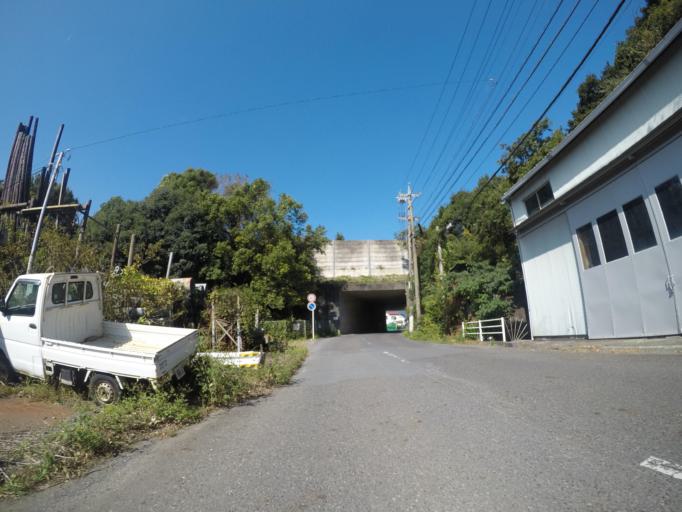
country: JP
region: Shizuoka
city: Shizuoka-shi
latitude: 35.0658
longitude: 138.5285
